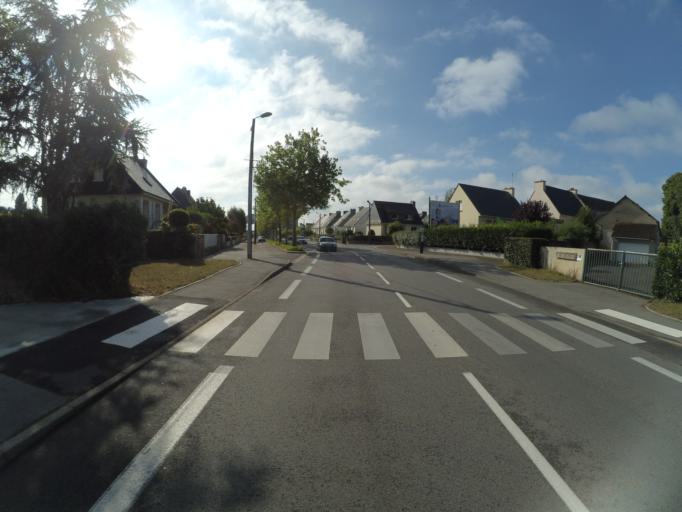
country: FR
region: Brittany
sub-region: Departement du Morbihan
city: Vannes
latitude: 47.6664
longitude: -2.7417
